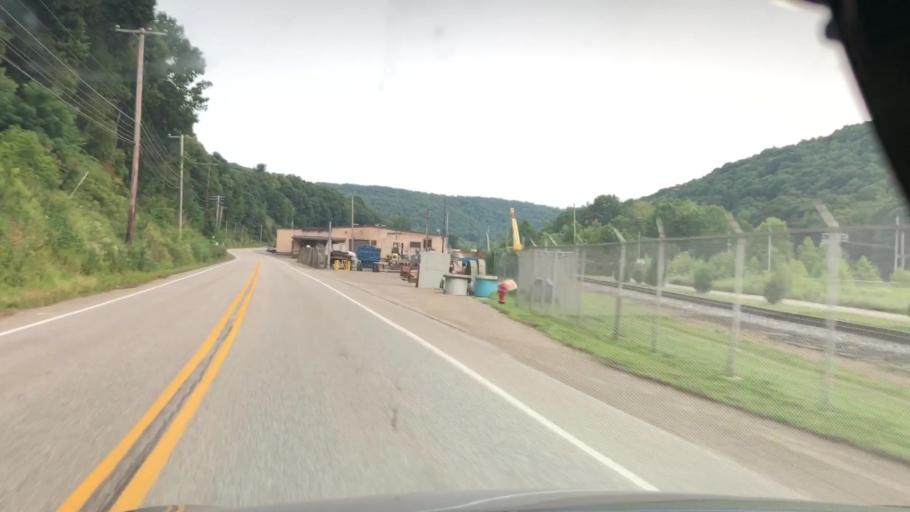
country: US
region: Pennsylvania
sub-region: Venango County
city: Hasson Heights
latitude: 41.4668
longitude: -79.6910
